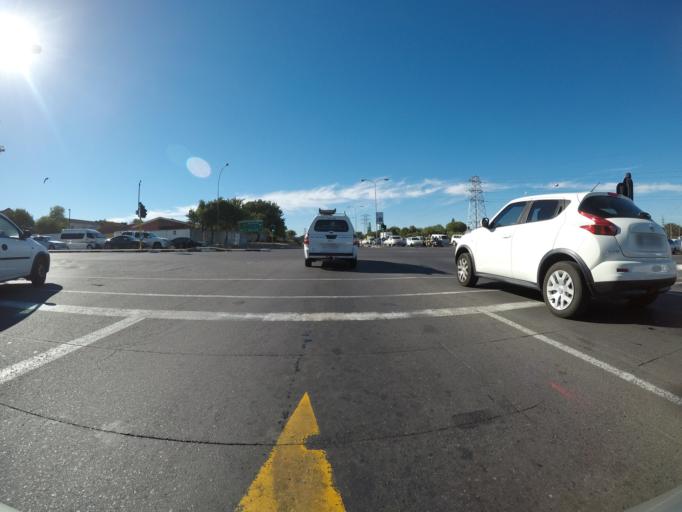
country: ZA
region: Western Cape
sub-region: City of Cape Town
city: Kraaifontein
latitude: -33.8880
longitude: 18.6715
